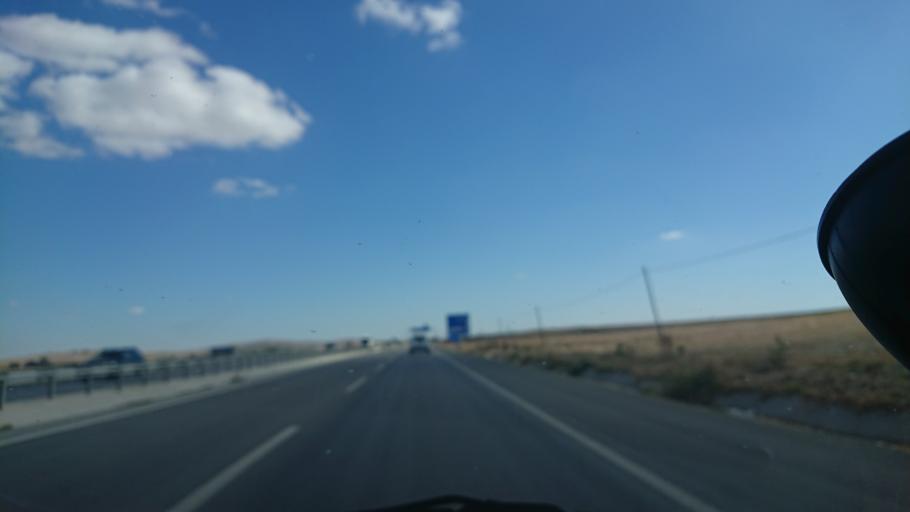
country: TR
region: Eskisehir
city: Mahmudiye
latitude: 39.5225
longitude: 30.9579
